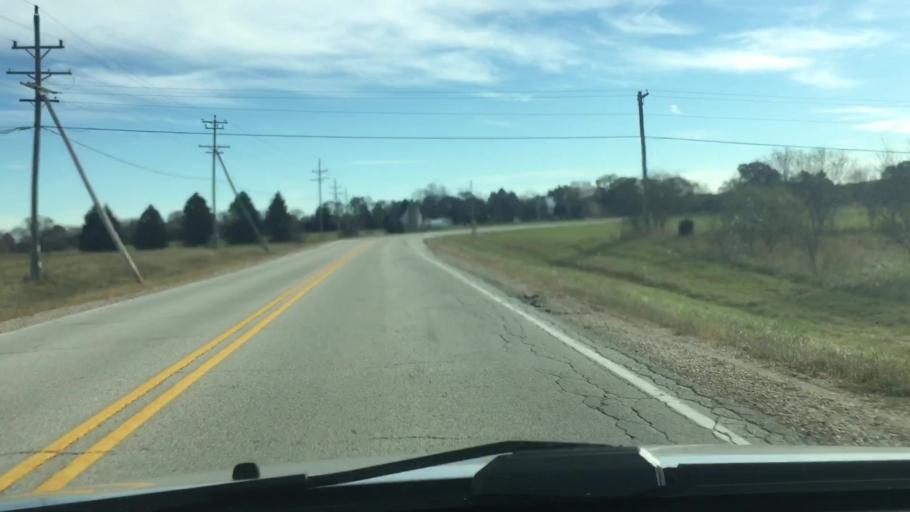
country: US
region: Wisconsin
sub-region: Waukesha County
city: North Prairie
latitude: 42.9448
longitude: -88.3823
